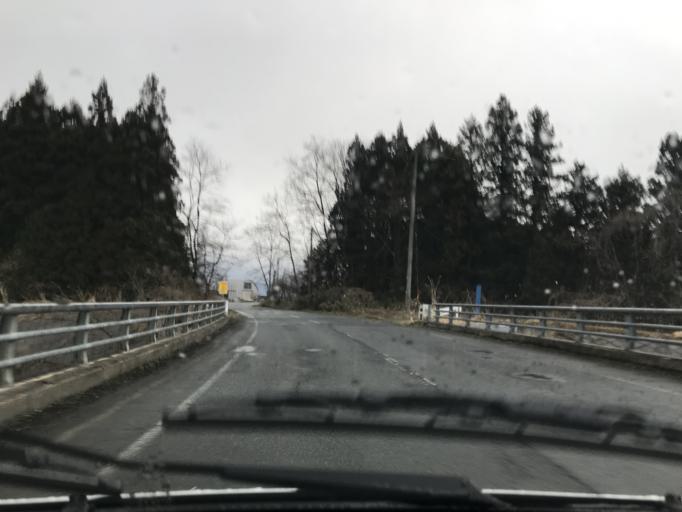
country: JP
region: Iwate
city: Mizusawa
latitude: 39.2004
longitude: 141.0873
